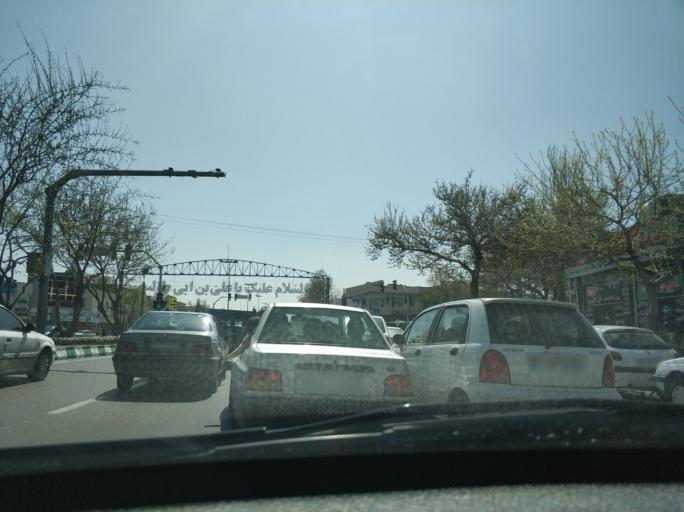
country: IR
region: Razavi Khorasan
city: Mashhad
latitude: 36.2627
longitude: 59.6039
